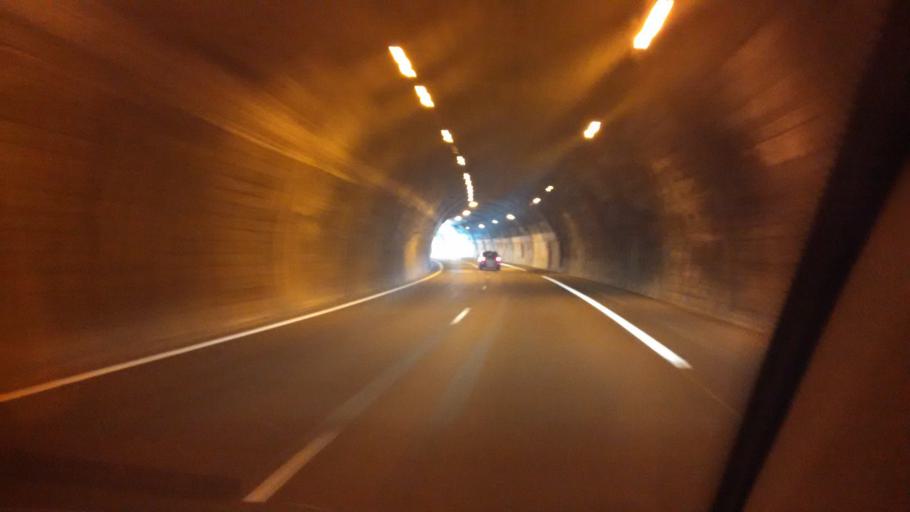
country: FR
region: Provence-Alpes-Cote d'Azur
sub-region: Departement des Alpes-Maritimes
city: Menton
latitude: 43.7888
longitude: 7.5283
